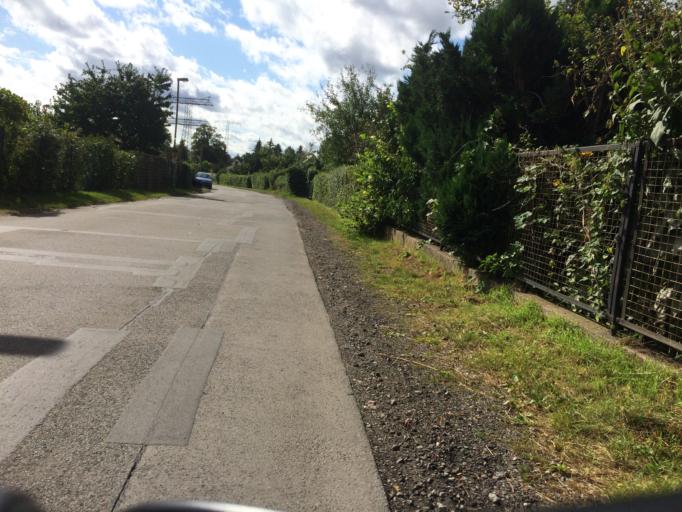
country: DE
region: Berlin
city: Weissensee
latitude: 52.5696
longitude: 13.4596
